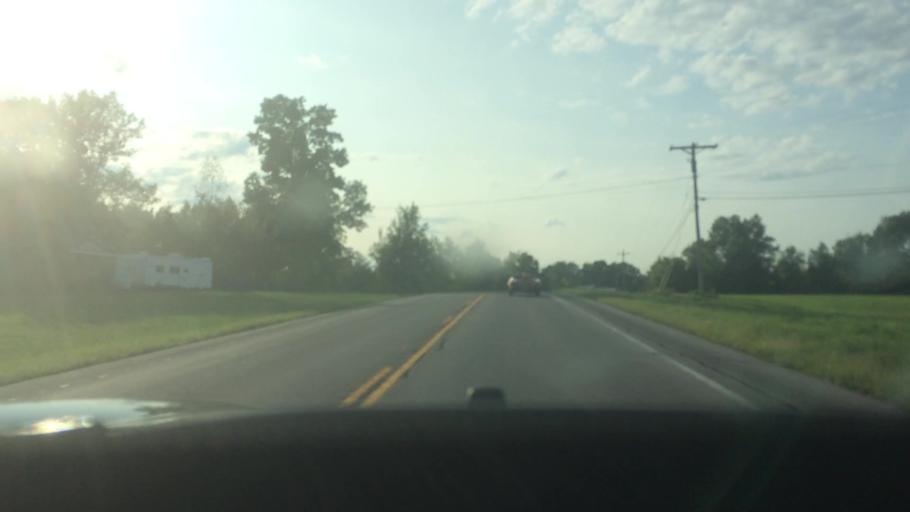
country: US
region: New York
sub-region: St. Lawrence County
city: Canton
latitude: 44.6370
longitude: -75.2750
